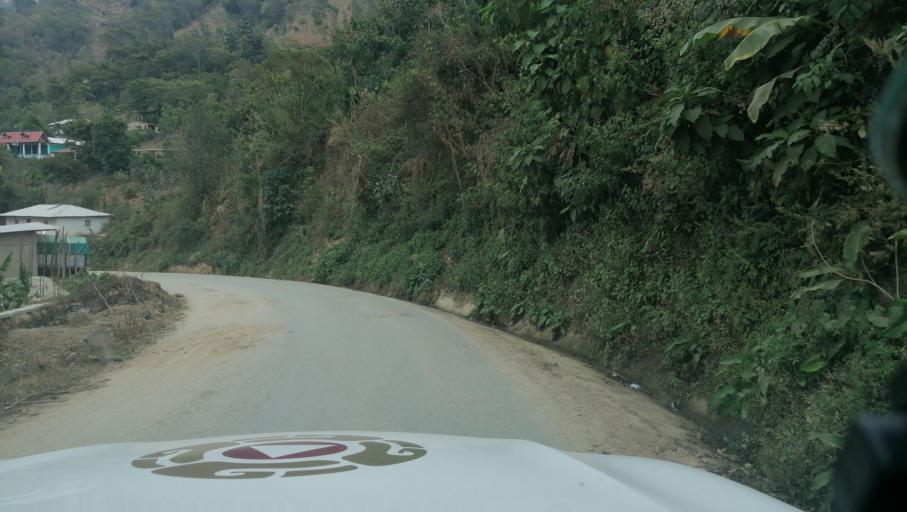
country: GT
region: San Marcos
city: Tacana
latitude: 15.2072
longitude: -92.1939
